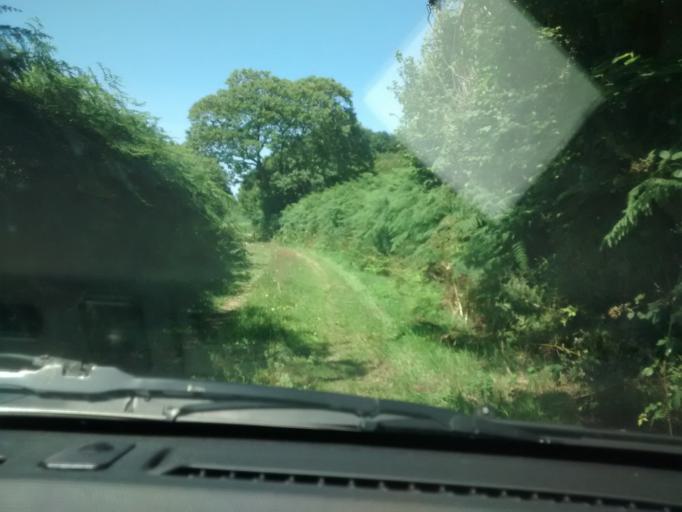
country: FR
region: Brittany
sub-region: Departement des Cotes-d'Armor
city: Trevou-Treguignec
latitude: 48.7777
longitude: -3.3367
